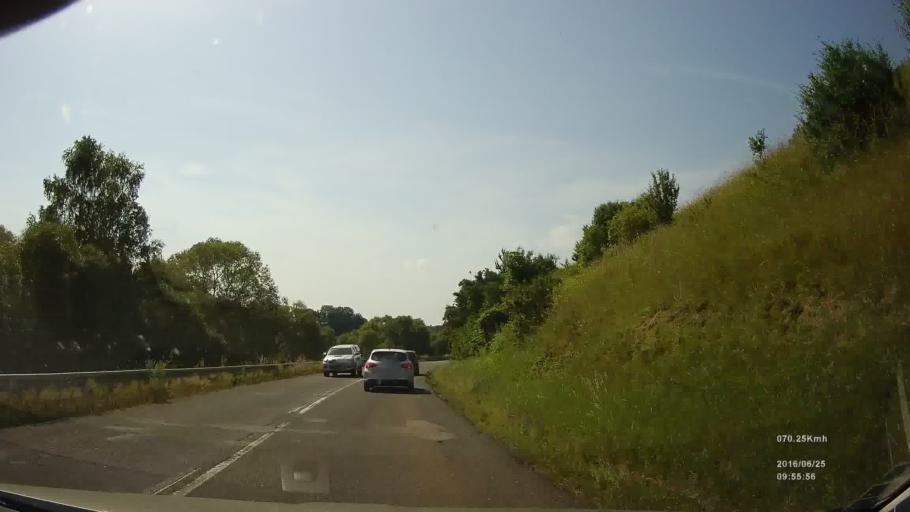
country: SK
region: Banskobystricky
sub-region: Okres Banska Bystrica
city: Banska Bystrica
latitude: 48.6811
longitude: 19.2194
